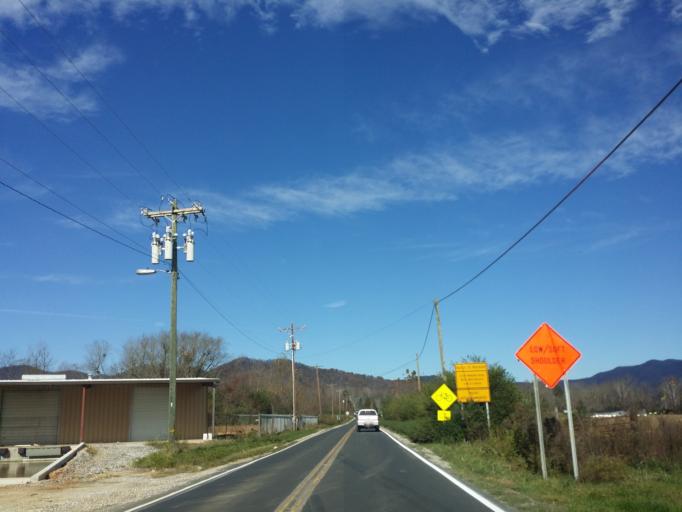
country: US
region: North Carolina
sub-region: McDowell County
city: West Marion
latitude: 35.6928
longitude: -82.0626
